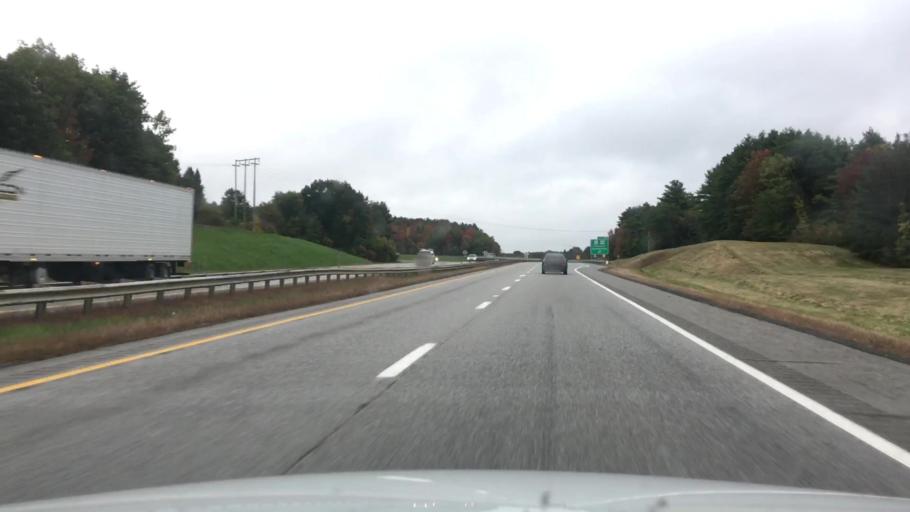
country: US
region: Maine
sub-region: Cumberland County
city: Falmouth
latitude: 43.7272
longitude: -70.3034
